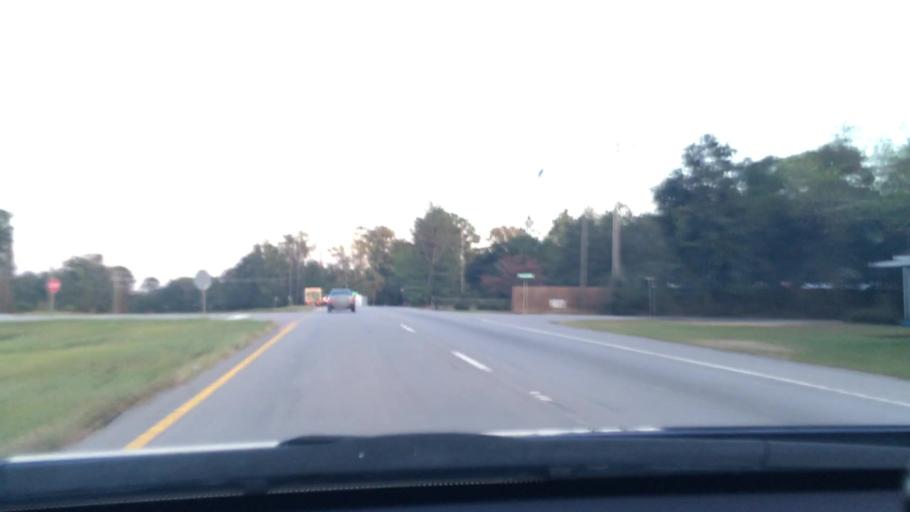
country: US
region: South Carolina
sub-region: Richland County
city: Gadsden
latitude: 33.9428
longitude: -80.7740
